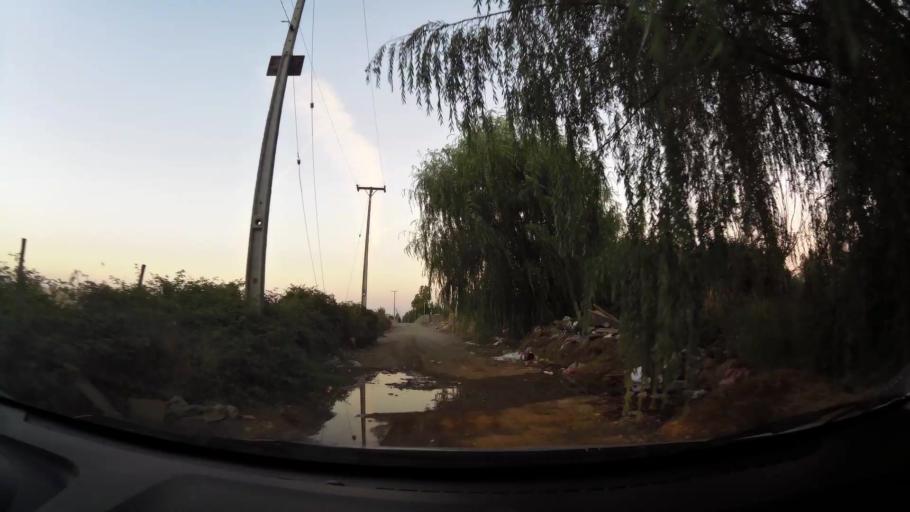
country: CL
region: Maule
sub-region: Provincia de Talca
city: Talca
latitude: -35.4510
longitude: -71.6267
